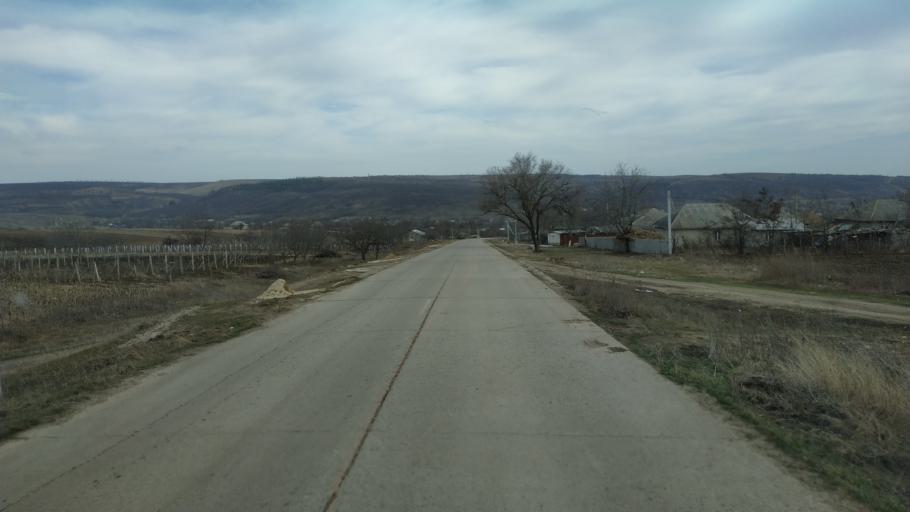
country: MD
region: Nisporeni
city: Nisporeni
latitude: 46.9292
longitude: 28.2553
